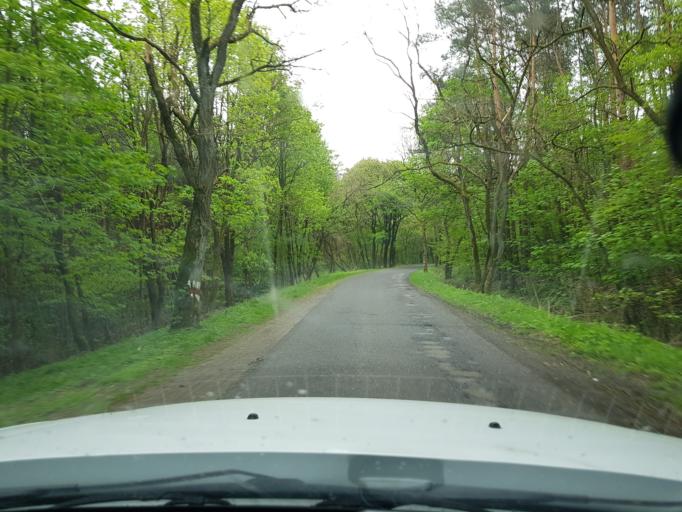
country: PL
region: West Pomeranian Voivodeship
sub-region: Powiat mysliborski
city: Debno
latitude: 52.6996
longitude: 14.6662
